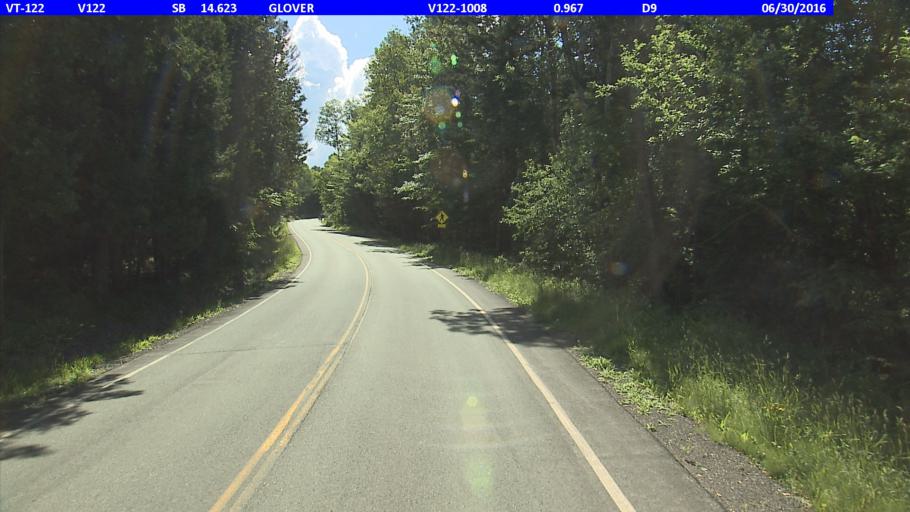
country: US
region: Vermont
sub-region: Caledonia County
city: Lyndonville
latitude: 44.6850
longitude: -72.1811
